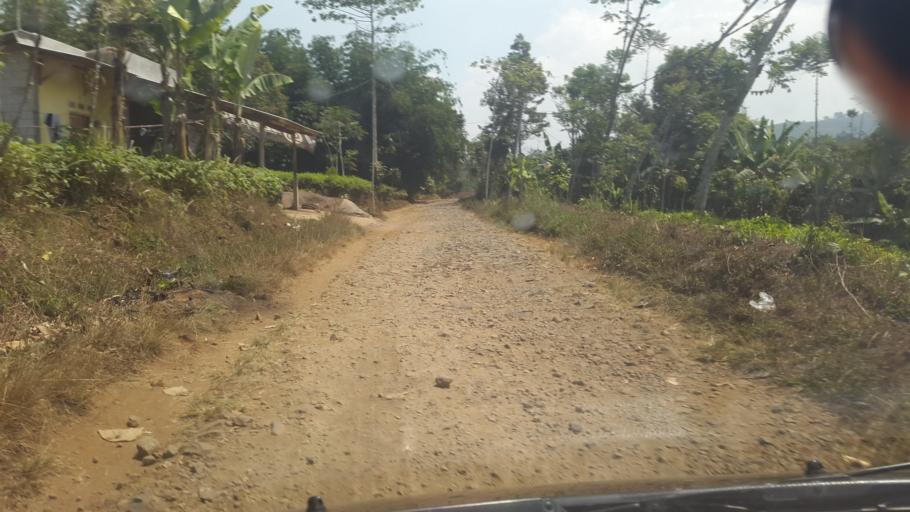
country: ID
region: West Java
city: Pasirhuni
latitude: -7.0273
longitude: 106.9897
